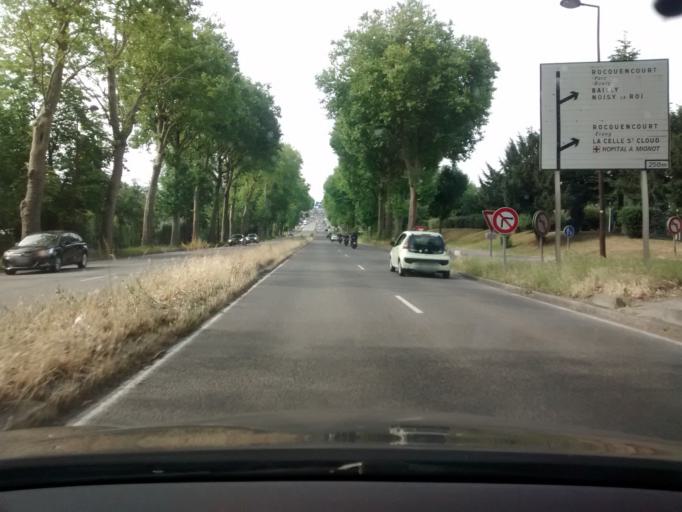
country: FR
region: Ile-de-France
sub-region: Departement des Yvelines
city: Rocquencourt
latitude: 48.8315
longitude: 2.1128
